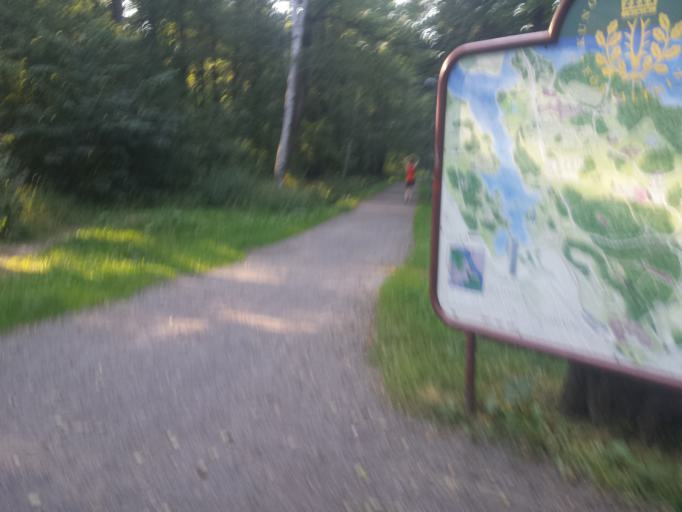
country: SE
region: Stockholm
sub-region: Stockholms Kommun
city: OEstermalm
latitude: 59.3477
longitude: 18.0774
